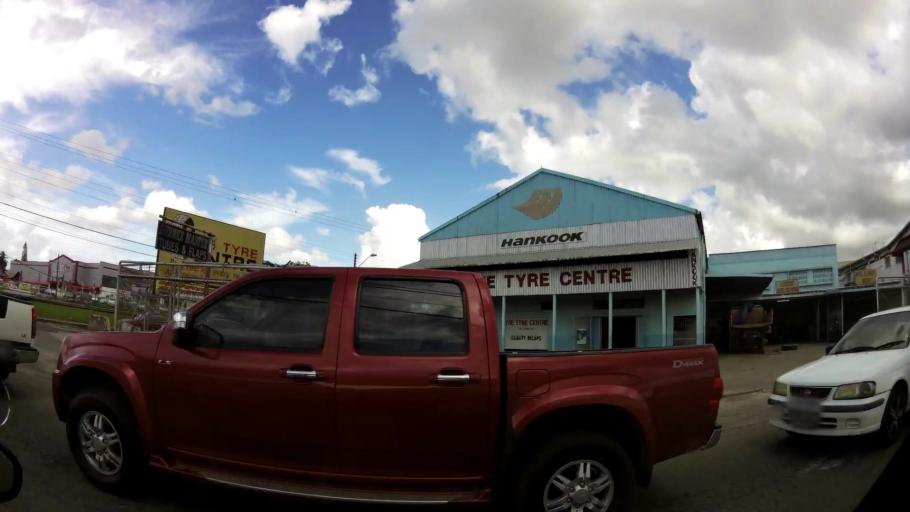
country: TT
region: City of San Fernando
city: San Fernando
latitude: 10.2646
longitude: -61.4592
